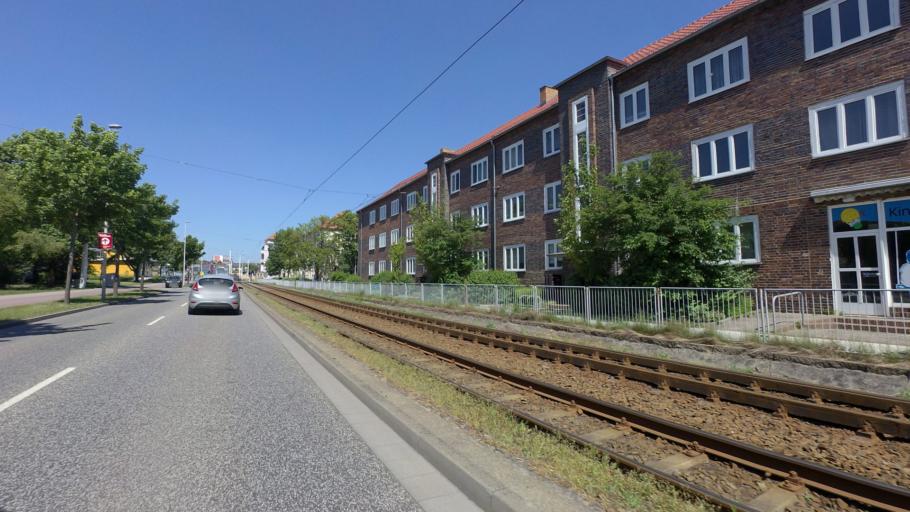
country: DE
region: Brandenburg
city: Cottbus
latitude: 51.7432
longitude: 14.3326
